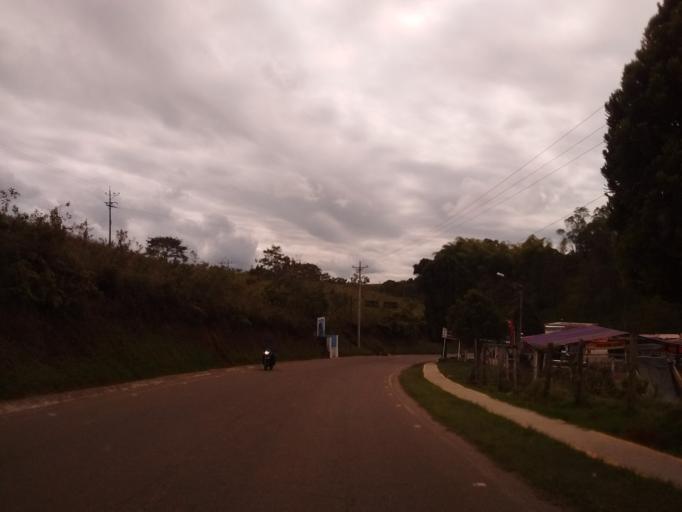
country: CO
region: Huila
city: Isnos
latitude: 1.9257
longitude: -76.2164
